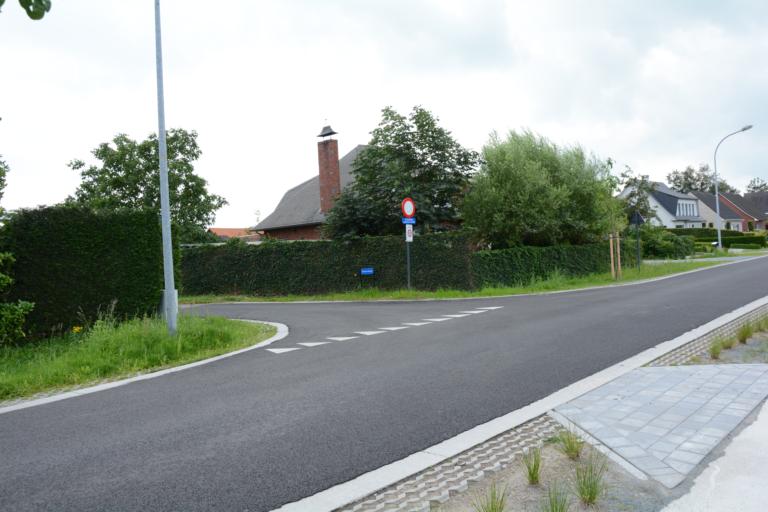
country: NL
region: North Brabant
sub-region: Gemeente Goirle
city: Goirle
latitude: 51.4524
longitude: 5.0301
